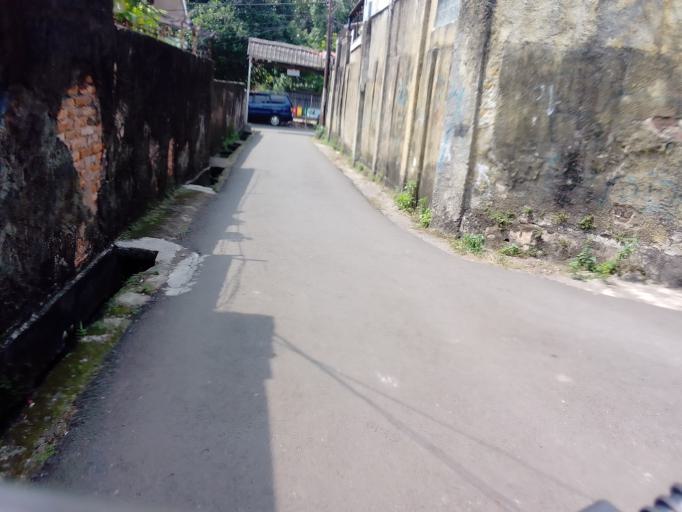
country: ID
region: Jakarta Raya
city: Jakarta
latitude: -6.2159
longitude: 106.8117
